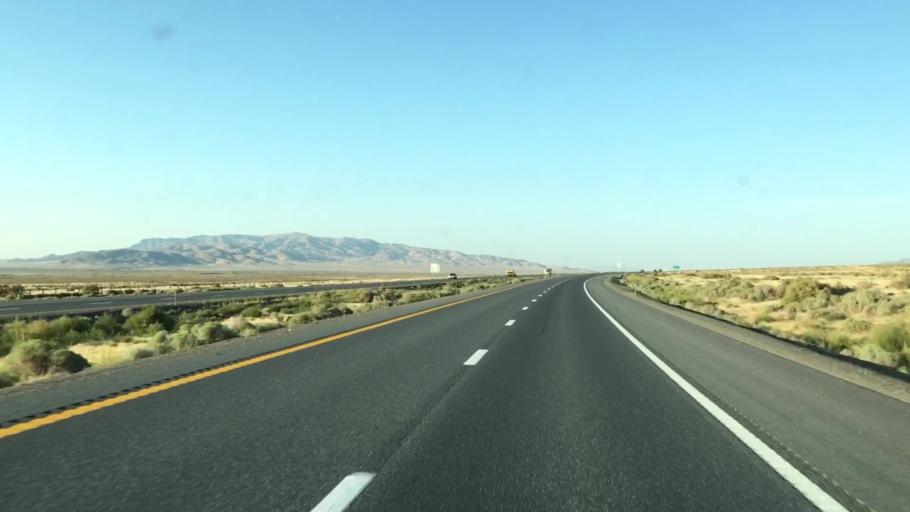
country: US
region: Nevada
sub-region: Pershing County
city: Lovelock
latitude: 40.6016
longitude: -118.2502
